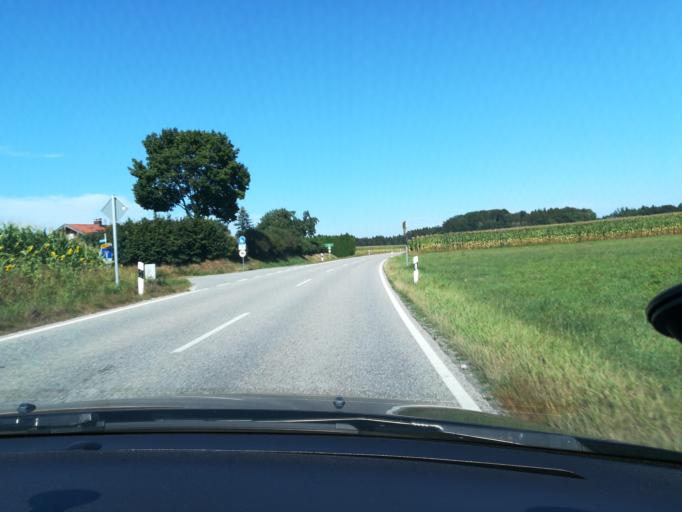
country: DE
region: Bavaria
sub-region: Upper Bavaria
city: Eggstatt
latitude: 47.9164
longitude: 12.3961
